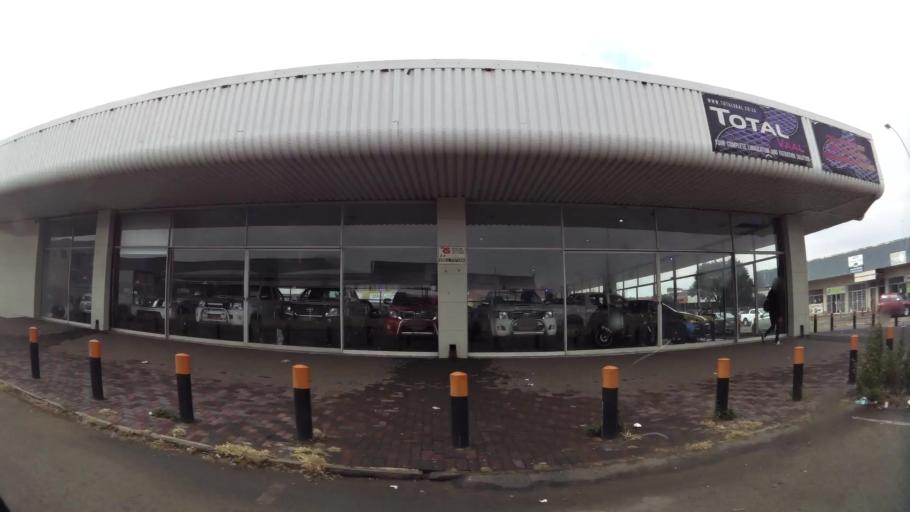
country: ZA
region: Gauteng
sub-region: Sedibeng District Municipality
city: Vanderbijlpark
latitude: -26.6976
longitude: 27.8335
